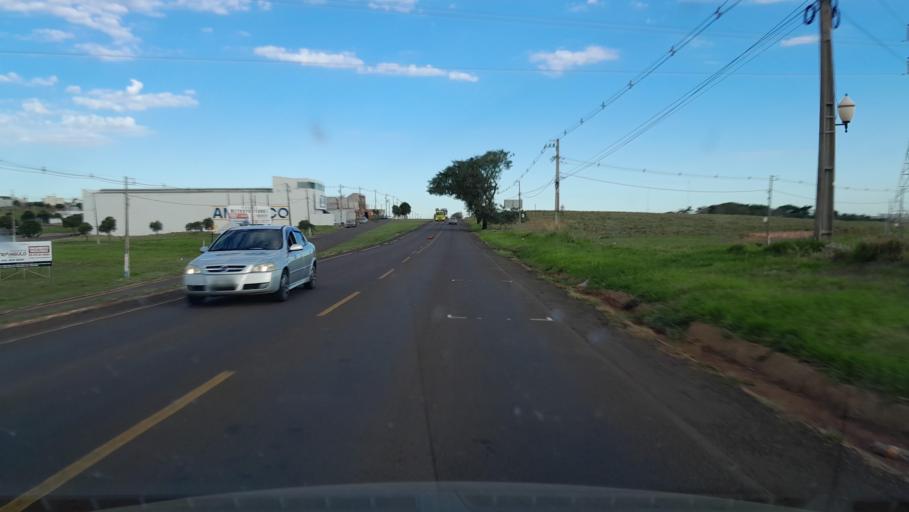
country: BR
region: Parana
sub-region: Umuarama
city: Umuarama
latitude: -23.7581
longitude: -53.2714
